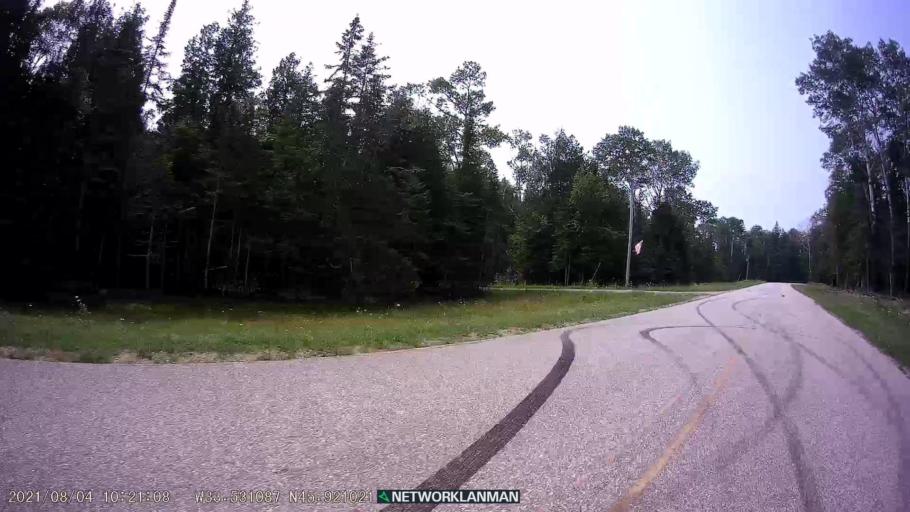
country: CA
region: Ontario
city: Thessalon
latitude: 45.9210
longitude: -83.5318
